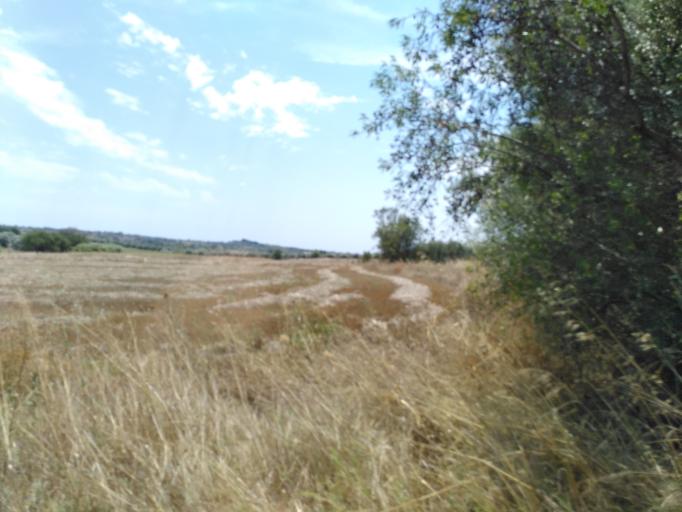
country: GR
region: Central Macedonia
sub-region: Nomos Thessalonikis
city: Epanomi
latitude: 40.4323
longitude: 22.9092
